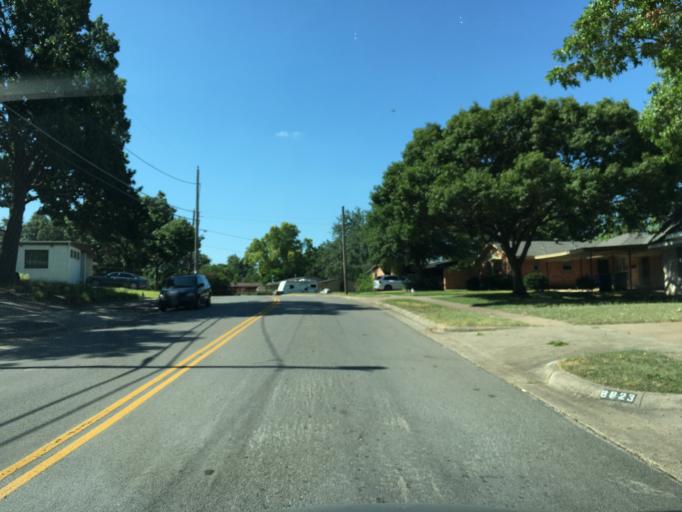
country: US
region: Texas
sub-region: Dallas County
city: Garland
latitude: 32.8696
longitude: -96.6939
